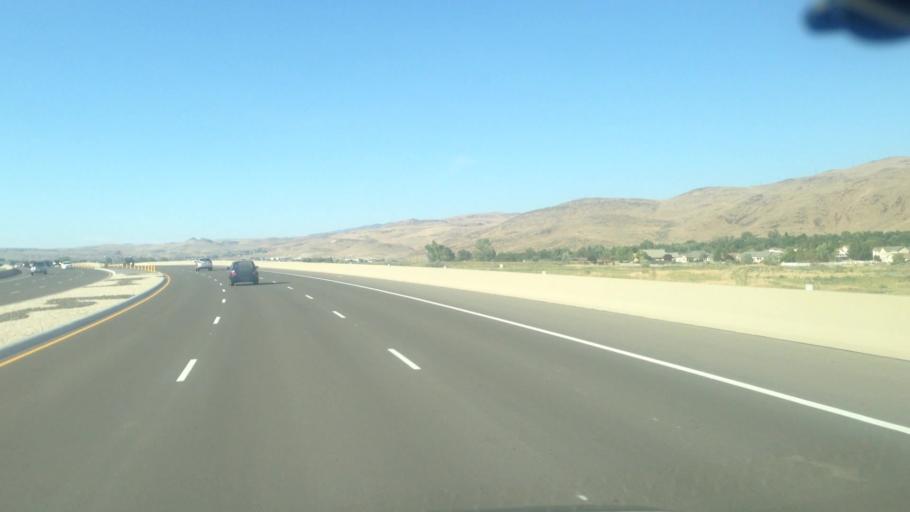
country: US
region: Nevada
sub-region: Washoe County
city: Sparks
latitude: 39.4897
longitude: -119.7332
